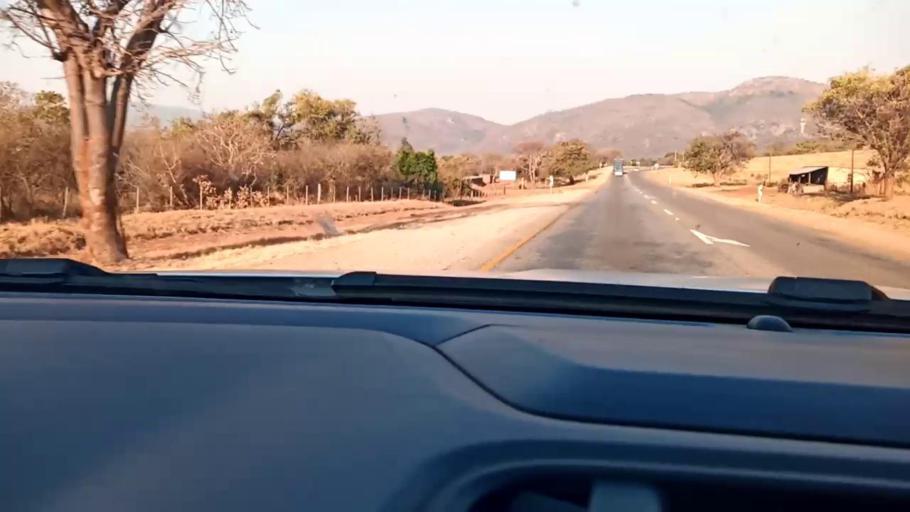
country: ZA
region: Limpopo
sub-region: Mopani District Municipality
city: Duiwelskloof
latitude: -23.6450
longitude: 30.1645
